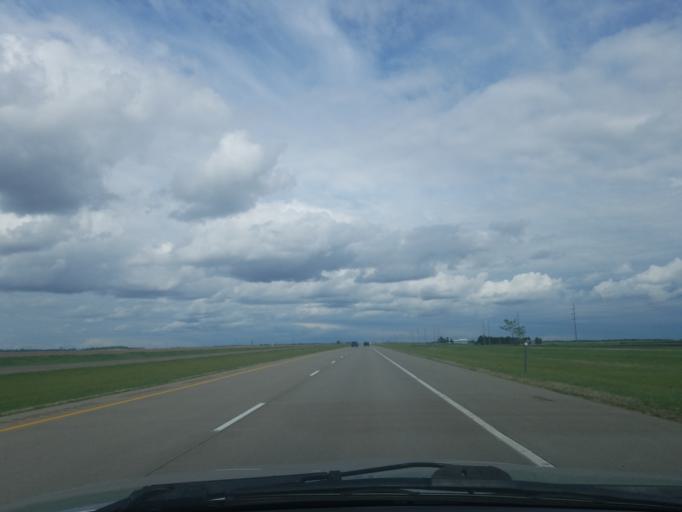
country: US
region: North Dakota
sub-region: Cass County
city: Casselton
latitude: 46.8766
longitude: -97.1557
